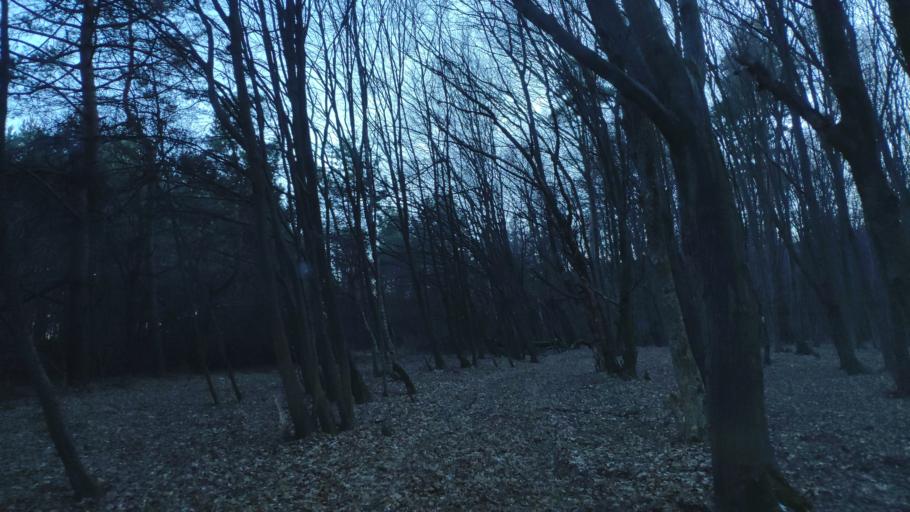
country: SK
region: Kosicky
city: Kosice
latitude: 48.8450
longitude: 21.2454
